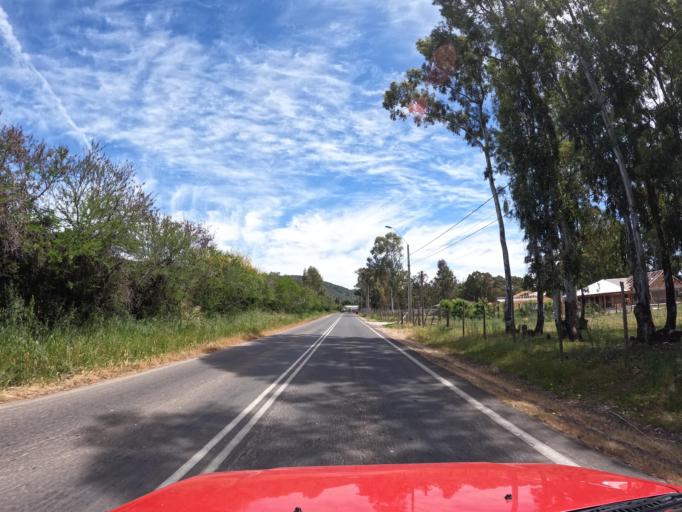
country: CL
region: Maule
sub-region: Provincia de Talca
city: Talca
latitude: -35.1170
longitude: -71.6427
